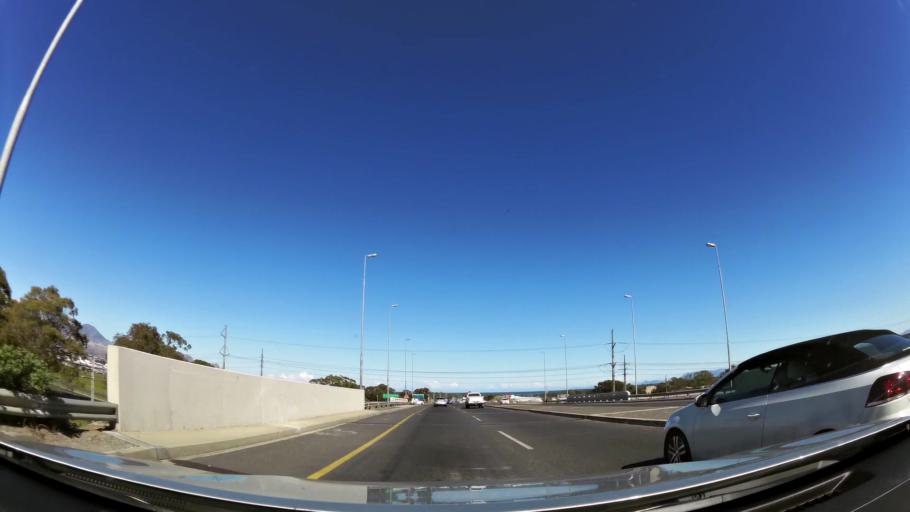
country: ZA
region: Western Cape
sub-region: Cape Winelands District Municipality
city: Stellenbosch
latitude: -34.0744
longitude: 18.8225
